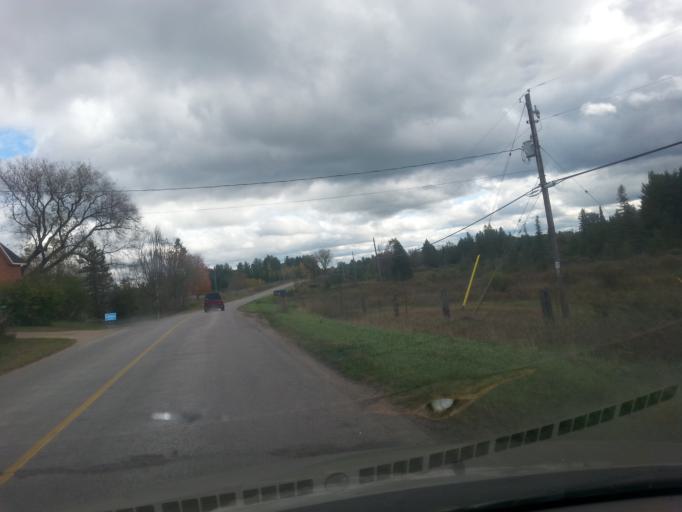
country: CA
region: Ontario
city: Pembroke
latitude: 45.5199
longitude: -77.0585
